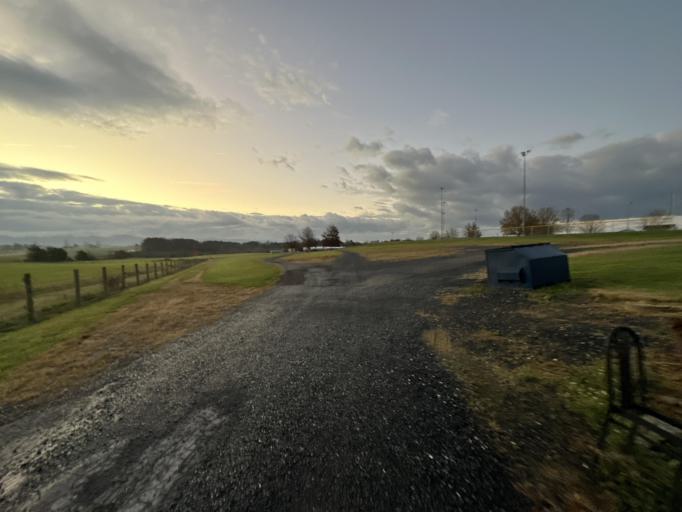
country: US
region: Virginia
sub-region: Augusta County
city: Weyers Cave
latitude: 38.2869
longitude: -78.9082
